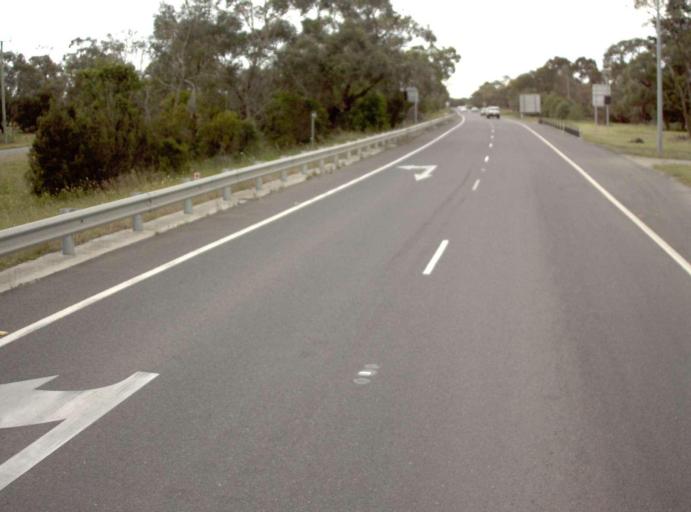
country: AU
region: Victoria
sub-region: Casey
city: Blind Bight
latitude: -38.1923
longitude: 145.3503
